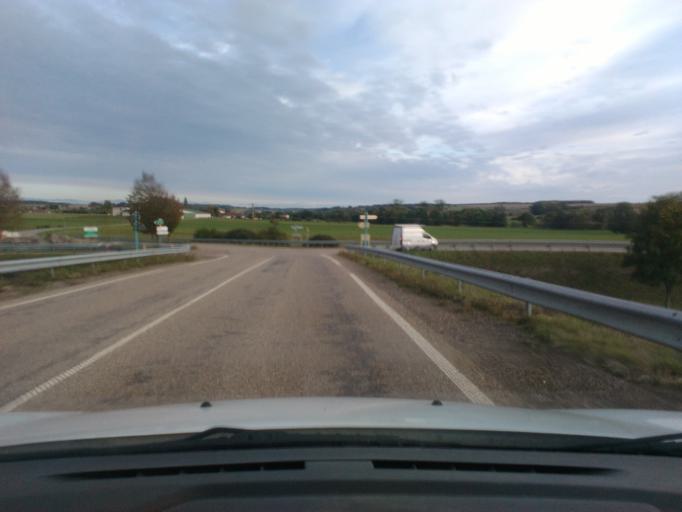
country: FR
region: Lorraine
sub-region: Departement des Vosges
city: Darnieulles
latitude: 48.2192
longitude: 6.2451
